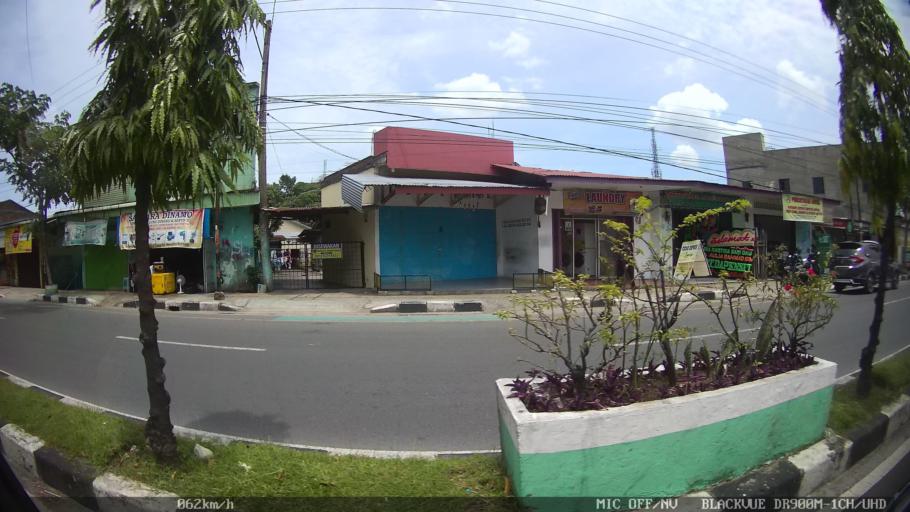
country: ID
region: North Sumatra
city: Sunggal
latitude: 3.5524
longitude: 98.6309
